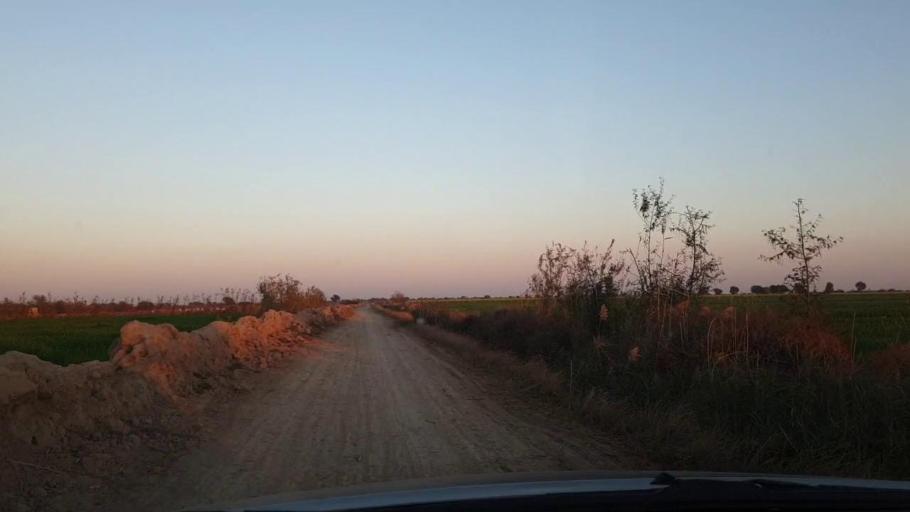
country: PK
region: Sindh
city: Tando Mittha Khan
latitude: 25.8565
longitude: 69.1934
